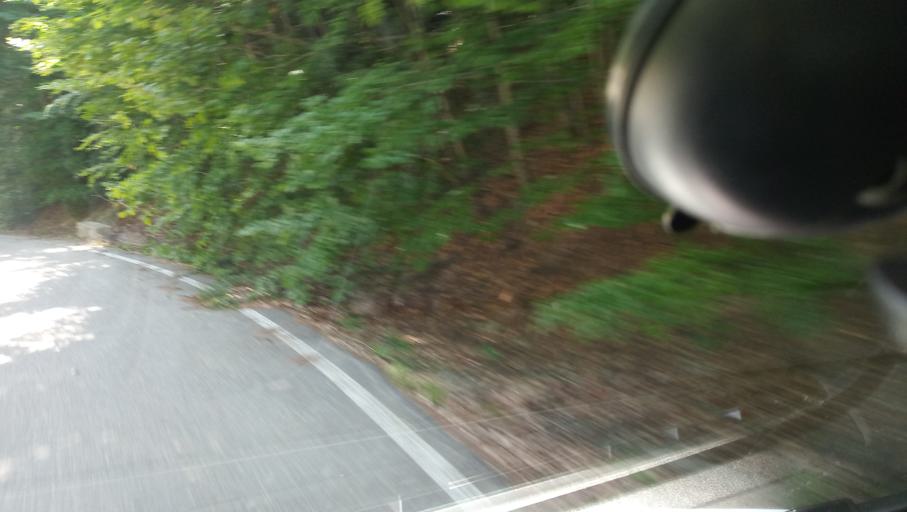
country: RO
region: Mehedinti
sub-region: Comuna Isverna
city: Isverna
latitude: 45.0412
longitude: 22.6186
